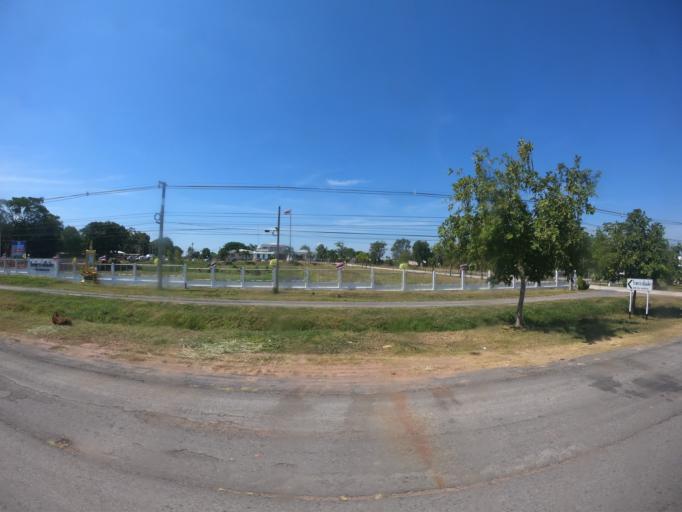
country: TH
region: Khon Kaen
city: Non Sila
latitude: 15.9787
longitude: 102.6951
